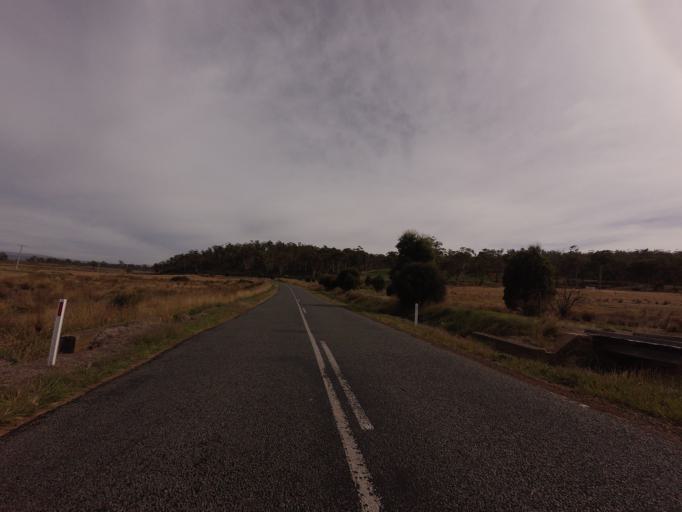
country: AU
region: Tasmania
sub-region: Brighton
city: Bridgewater
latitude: -42.3351
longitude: 147.4013
